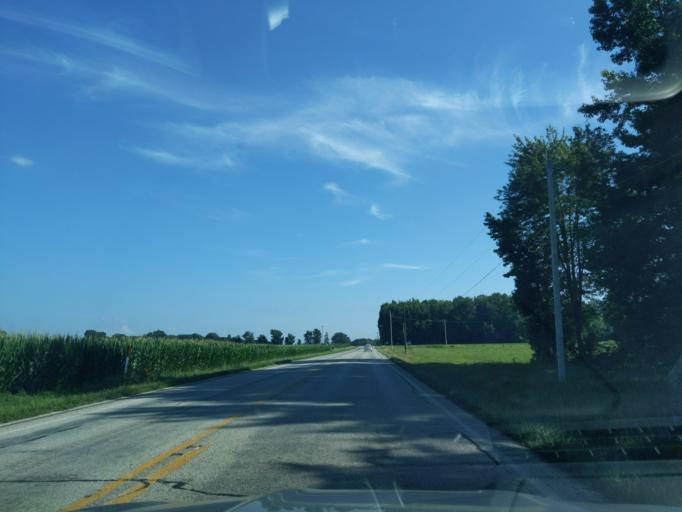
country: US
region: Indiana
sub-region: Ripley County
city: Osgood
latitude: 39.0982
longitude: -85.2772
